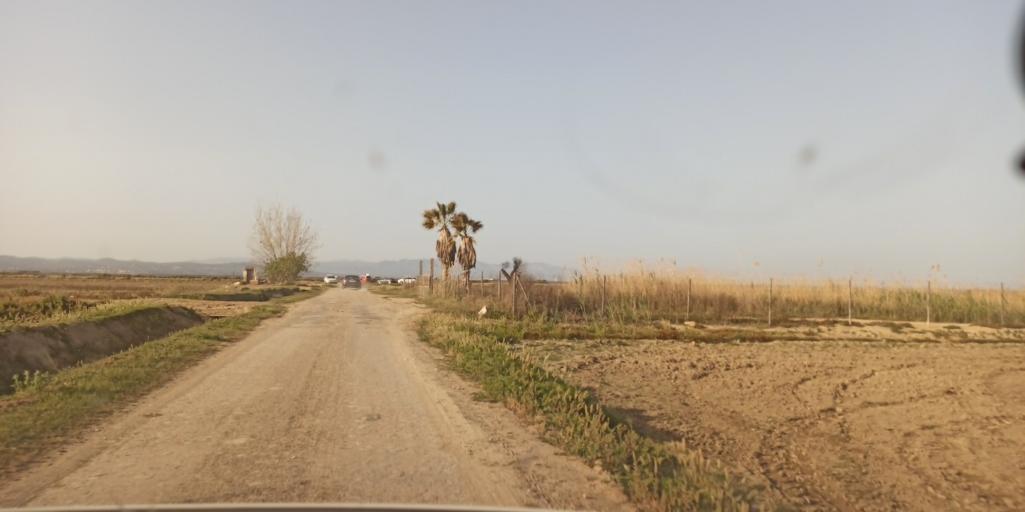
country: ES
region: Catalonia
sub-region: Provincia de Tarragona
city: Deltebre
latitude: 40.7613
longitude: 0.7543
